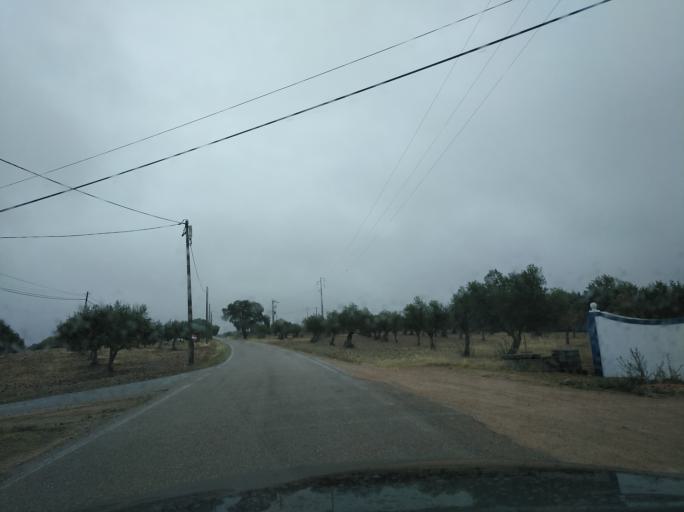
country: PT
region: Portalegre
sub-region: Campo Maior
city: Campo Maior
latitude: 38.9649
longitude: -7.0724
